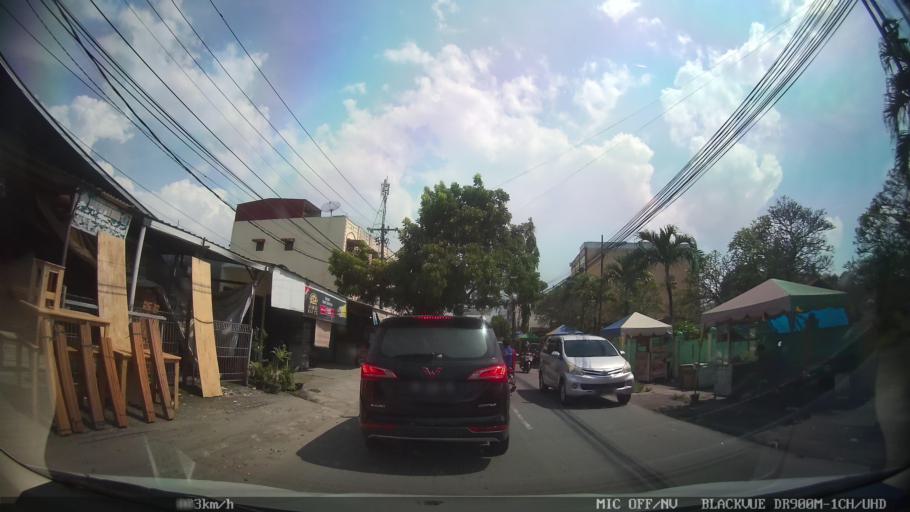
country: ID
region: North Sumatra
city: Medan
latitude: 3.6221
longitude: 98.6651
